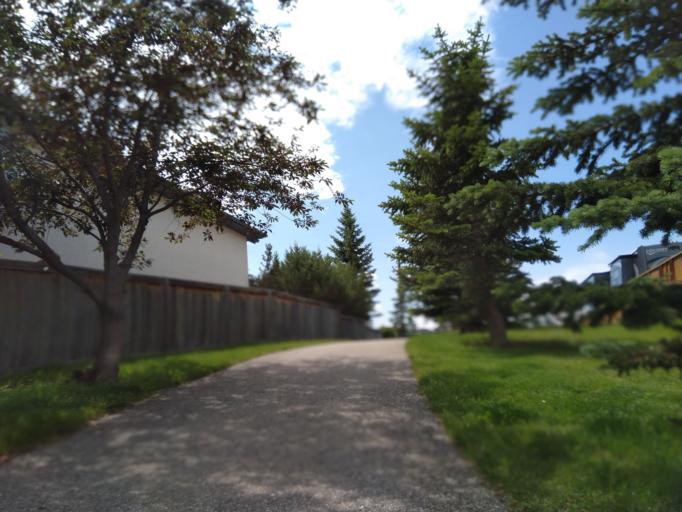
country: CA
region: Alberta
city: Cochrane
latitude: 51.1865
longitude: -114.5052
